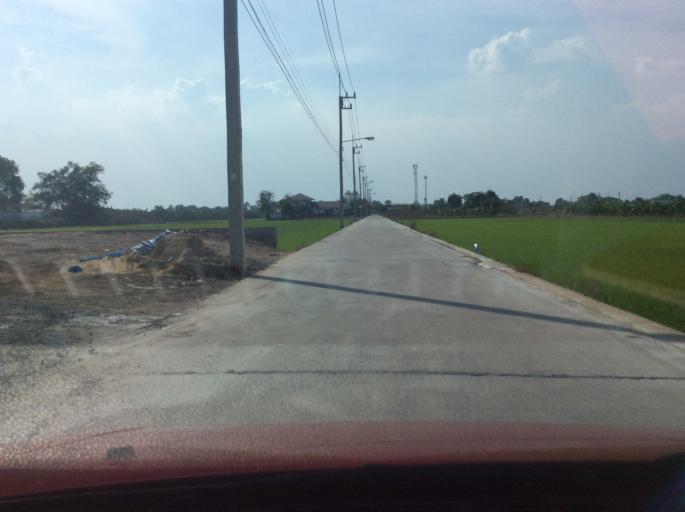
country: TH
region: Pathum Thani
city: Lam Luk Ka
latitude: 13.9677
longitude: 100.7343
